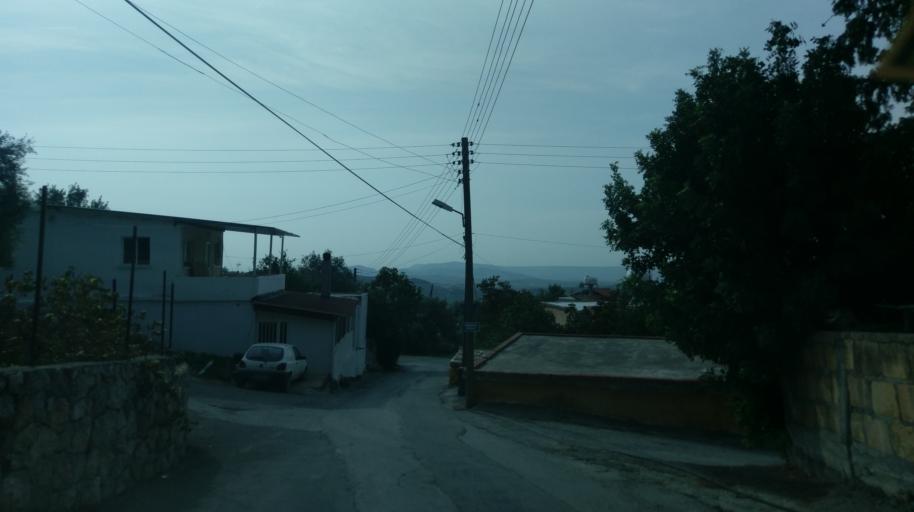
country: CY
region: Keryneia
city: Lapithos
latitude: 35.3122
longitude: 33.1409
